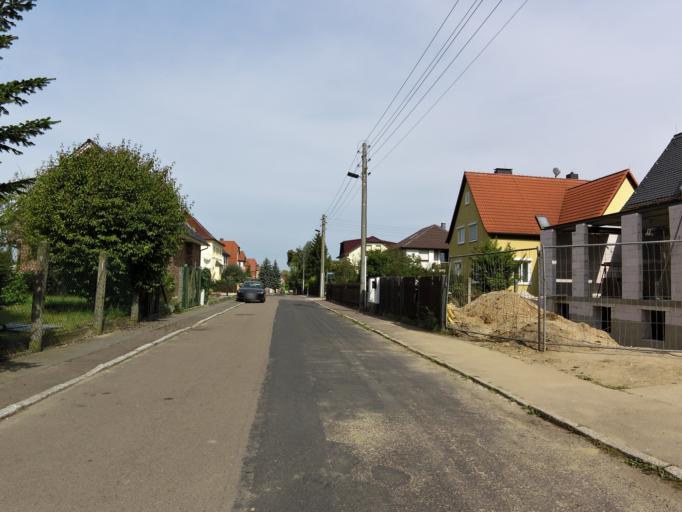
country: DE
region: Saxony
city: Schkeuditz
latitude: 51.3595
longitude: 12.2681
